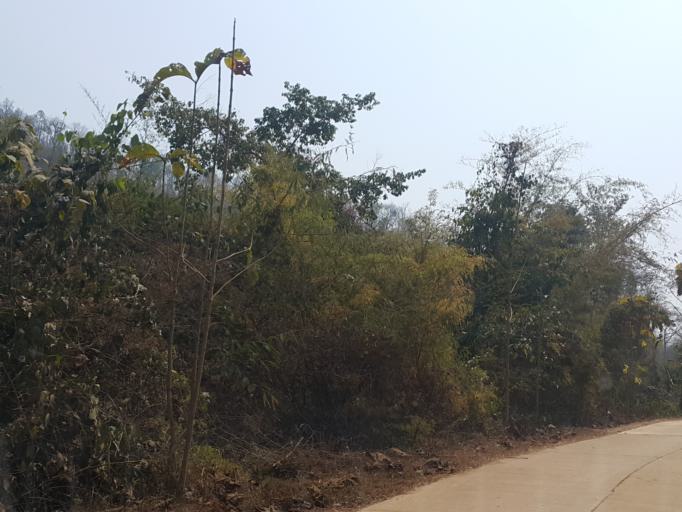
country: TH
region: Chiang Mai
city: Hang Dong
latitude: 18.7453
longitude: 98.8268
